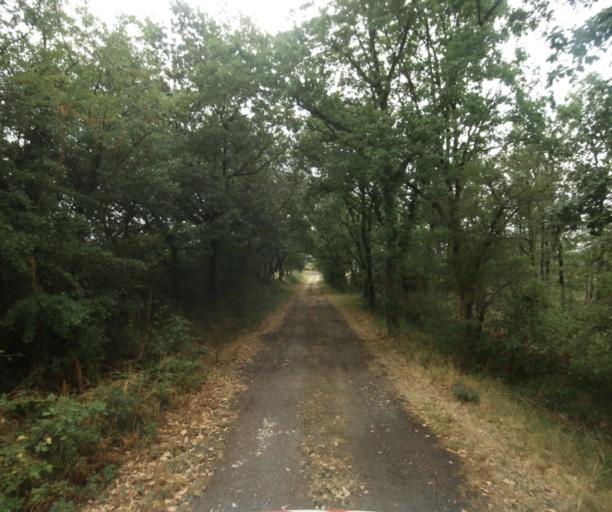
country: FR
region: Midi-Pyrenees
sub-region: Departement de la Haute-Garonne
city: Revel
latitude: 43.4403
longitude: 1.9803
